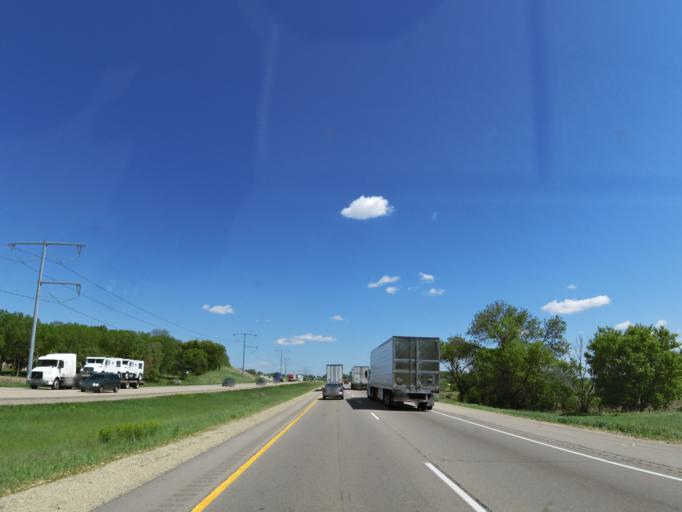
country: US
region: Wisconsin
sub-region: Dane County
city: Cottage Grove
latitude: 43.0041
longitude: -89.2079
